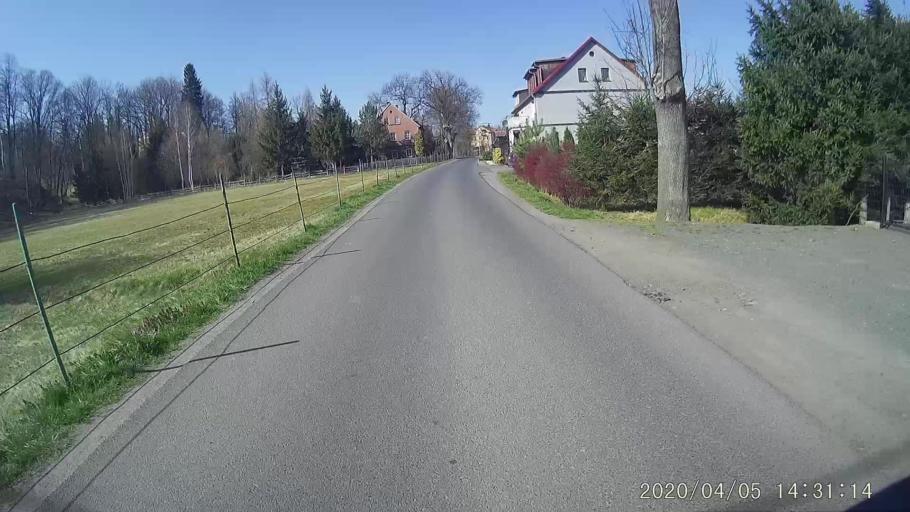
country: PL
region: Lower Silesian Voivodeship
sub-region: Powiat lubanski
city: Lesna
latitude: 51.0311
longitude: 15.2579
